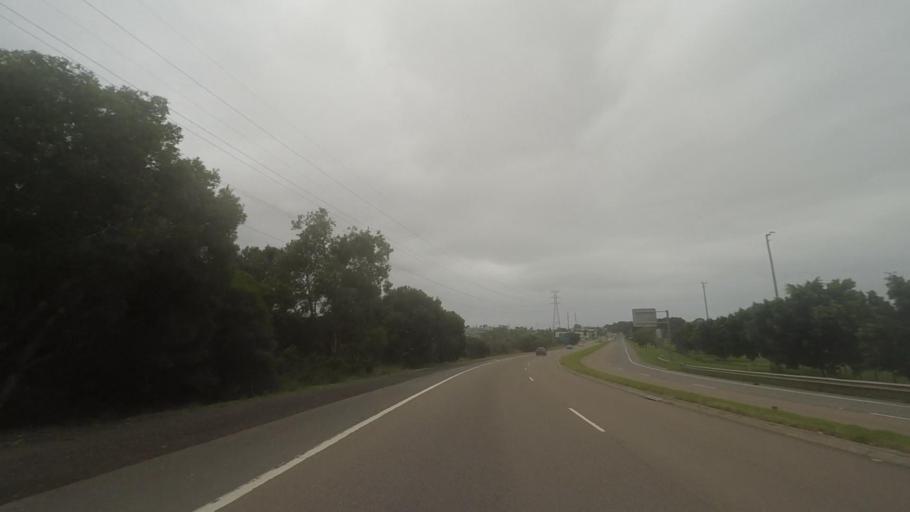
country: AU
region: New South Wales
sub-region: Newcastle
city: Mayfield West
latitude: -32.8823
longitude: 151.7212
